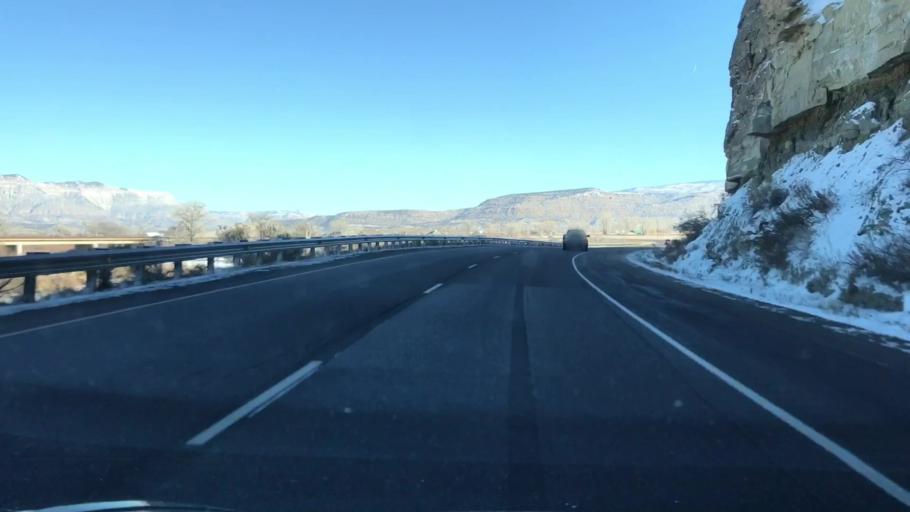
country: US
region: Colorado
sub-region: Mesa County
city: Palisade
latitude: 39.2793
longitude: -108.2370
